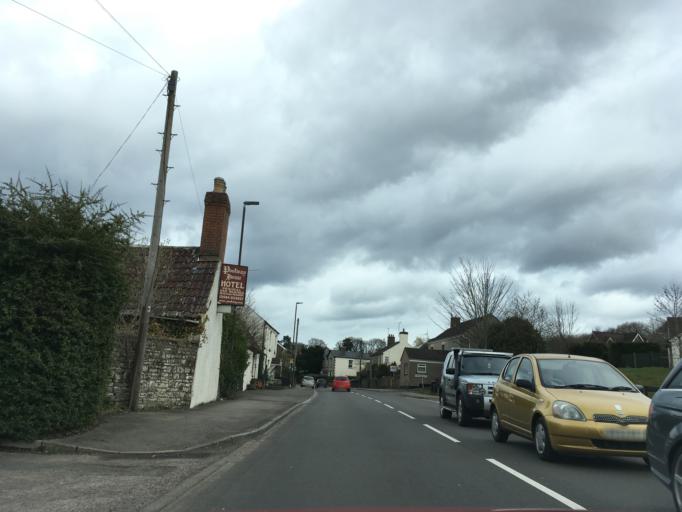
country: GB
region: England
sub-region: Gloucestershire
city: Coleford
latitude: 51.7957
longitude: -2.6126
